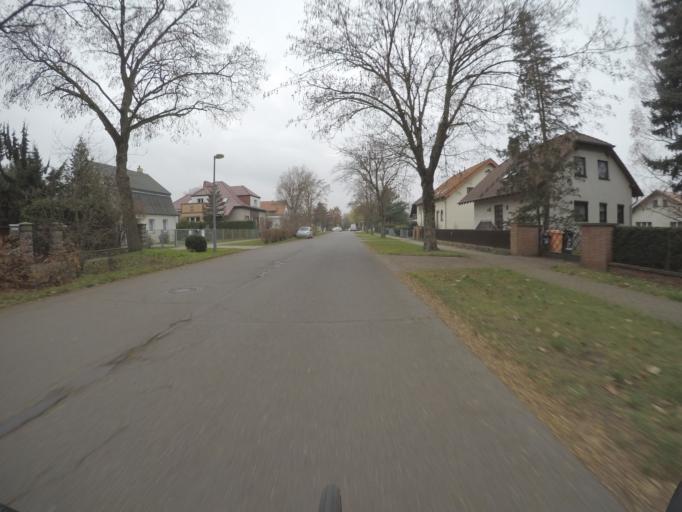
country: DE
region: Berlin
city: Biesdorf
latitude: 52.5016
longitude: 13.5563
